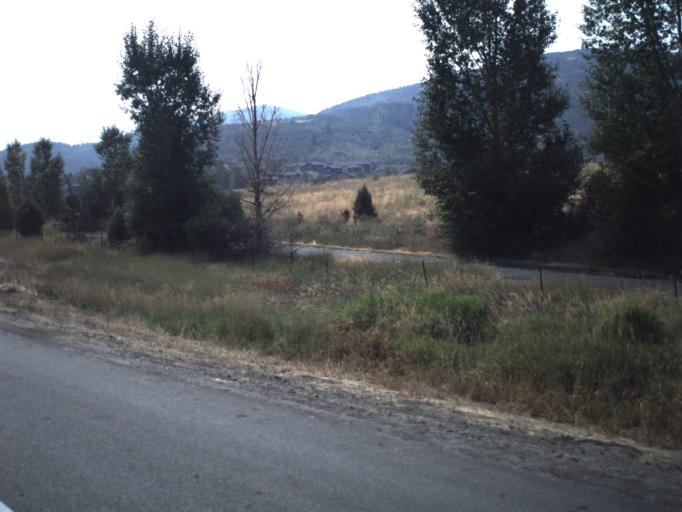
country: US
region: Utah
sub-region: Summit County
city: Snyderville
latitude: 40.7157
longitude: -111.5449
